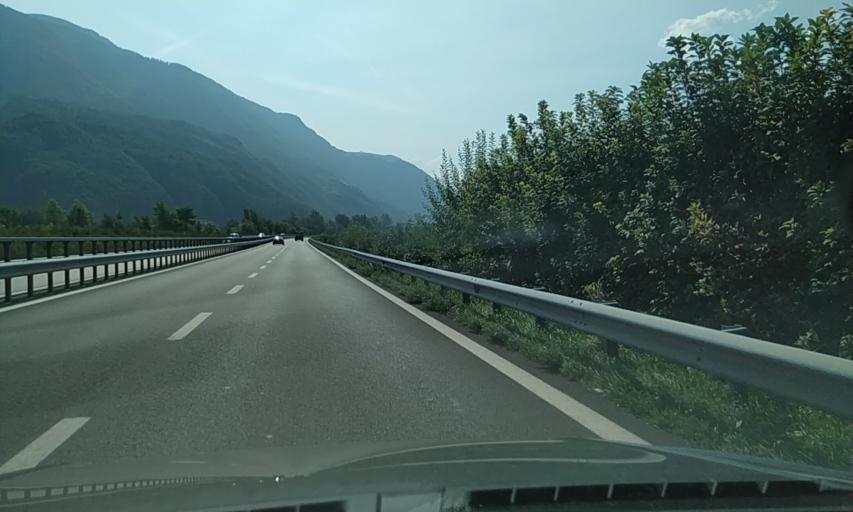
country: IT
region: Trentino-Alto Adige
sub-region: Bolzano
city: Sinigo
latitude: 46.6413
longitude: 11.1662
